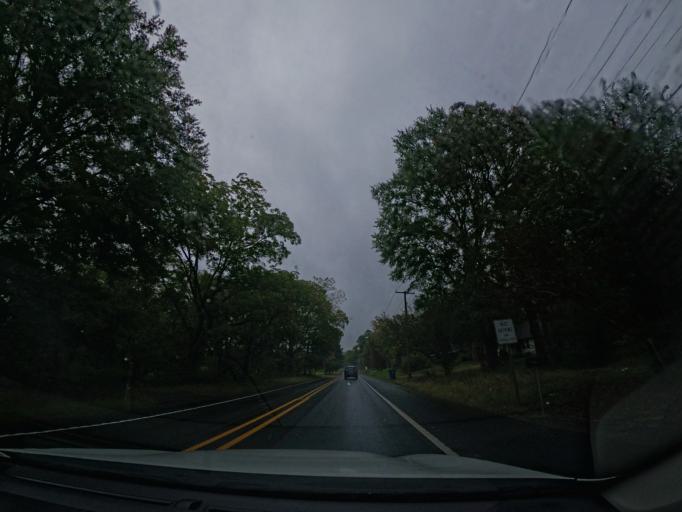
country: US
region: Louisiana
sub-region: Caddo Parish
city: Greenwood
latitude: 32.3736
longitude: -94.0394
